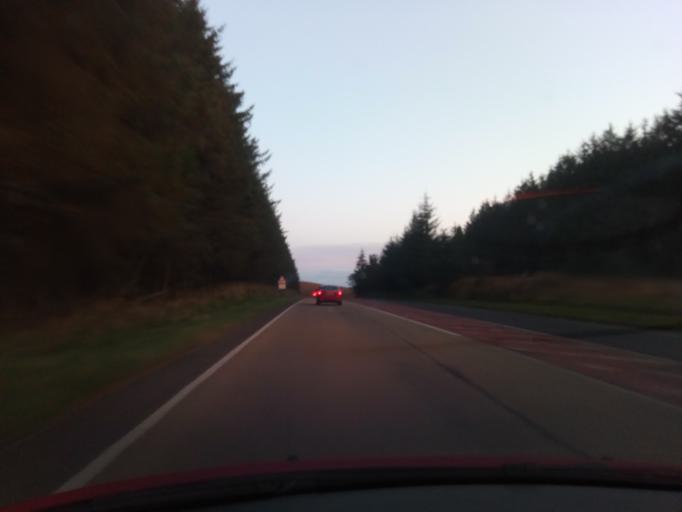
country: GB
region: Scotland
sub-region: East Lothian
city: Pencaitland
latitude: 55.8075
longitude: -2.8370
